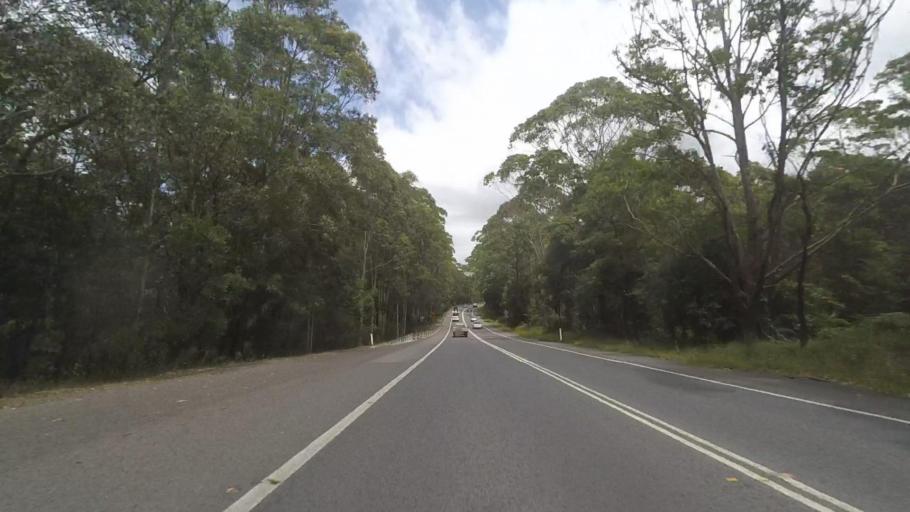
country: AU
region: New South Wales
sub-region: Shoalhaven Shire
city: Falls Creek
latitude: -35.0843
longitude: 150.5419
